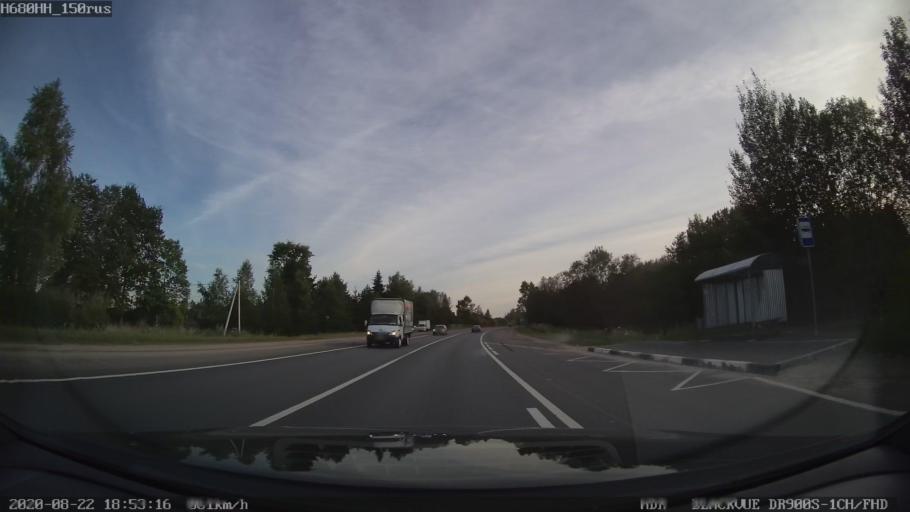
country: RU
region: Tverskaya
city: Rameshki
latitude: 57.2272
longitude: 36.0990
